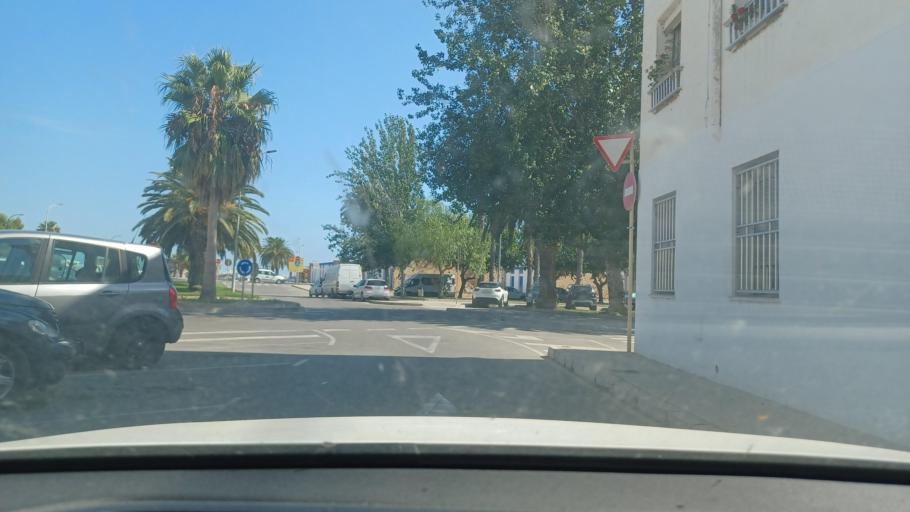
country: ES
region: Catalonia
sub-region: Provincia de Tarragona
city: Sant Carles de la Rapita
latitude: 40.6205
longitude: 0.5969
